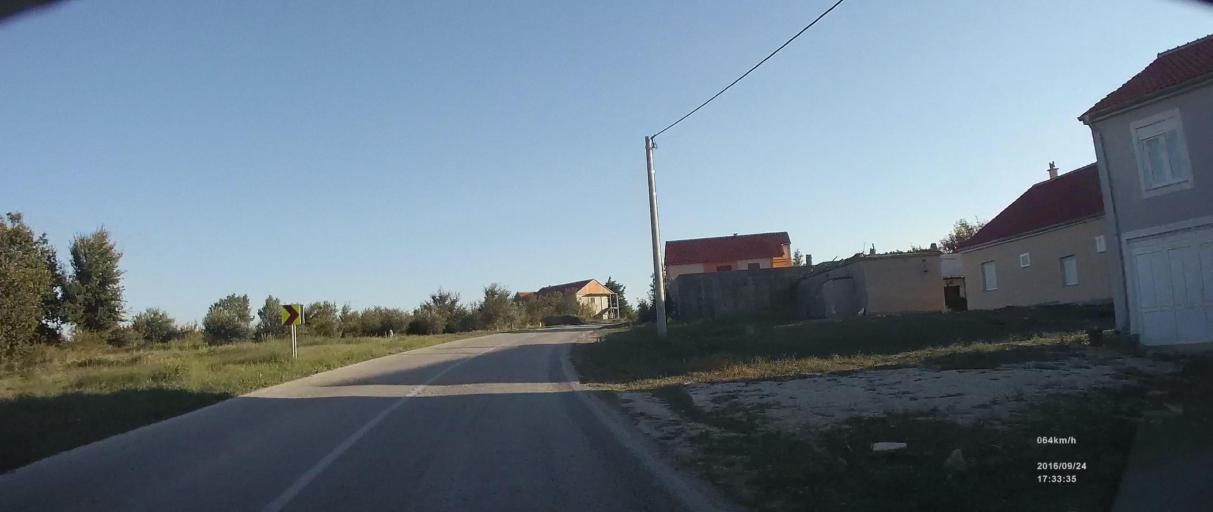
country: HR
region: Zadarska
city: Posedarje
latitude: 44.1730
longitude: 15.4575
